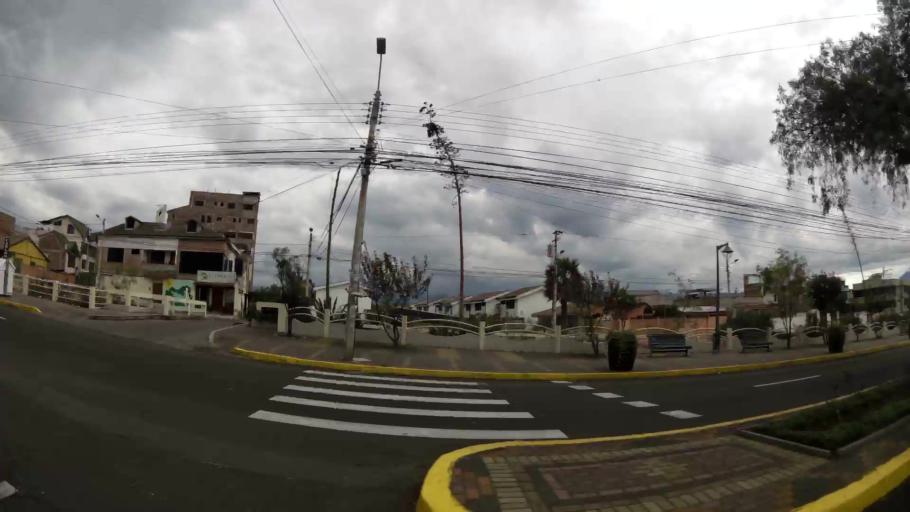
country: EC
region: Tungurahua
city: Ambato
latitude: -1.2335
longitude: -78.6139
